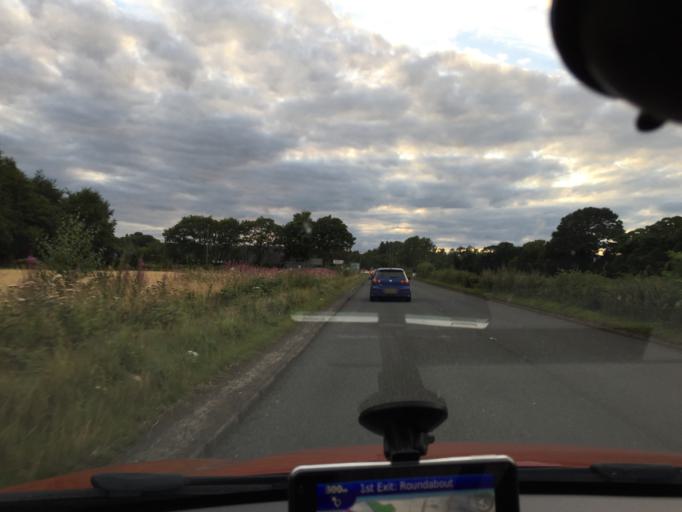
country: GB
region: Scotland
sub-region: Falkirk
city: Bonnybridge
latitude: 56.0119
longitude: -3.8654
